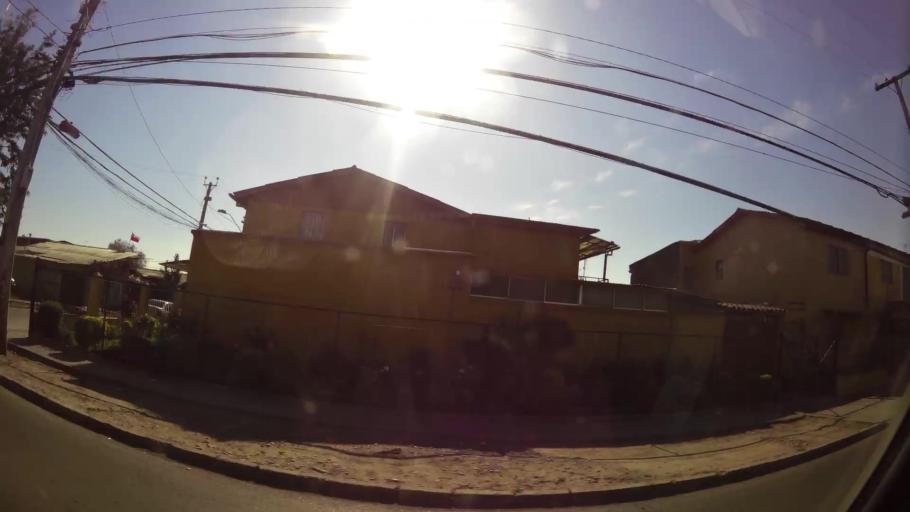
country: CL
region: Santiago Metropolitan
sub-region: Provincia de Santiago
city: Santiago
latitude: -33.5061
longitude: -70.6773
